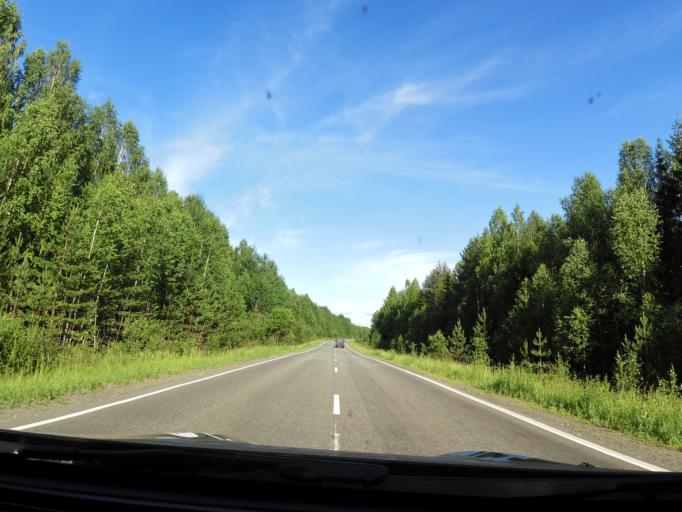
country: RU
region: Kirov
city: Chernaya Kholunitsa
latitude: 58.8684
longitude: 51.5582
